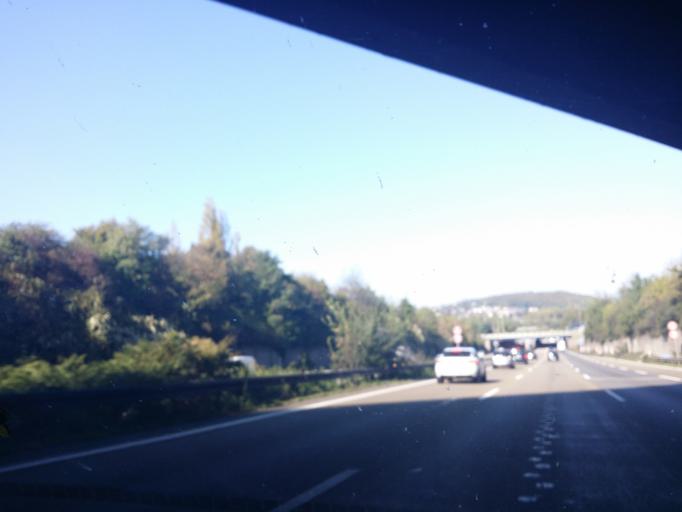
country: DE
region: North Rhine-Westphalia
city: Herdecke
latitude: 51.3863
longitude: 7.4388
